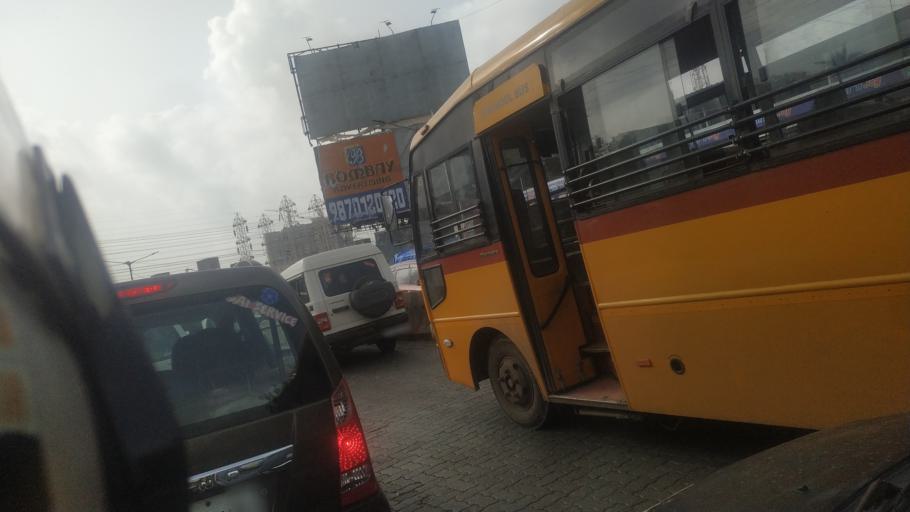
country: IN
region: Maharashtra
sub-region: Mumbai Suburban
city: Mumbai
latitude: 19.0462
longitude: 72.8632
